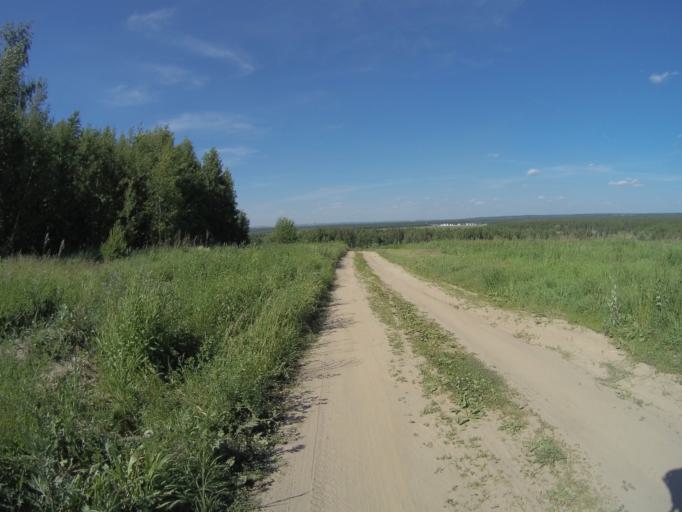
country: RU
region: Vladimir
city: Raduzhnyy
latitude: 55.9988
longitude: 40.3707
